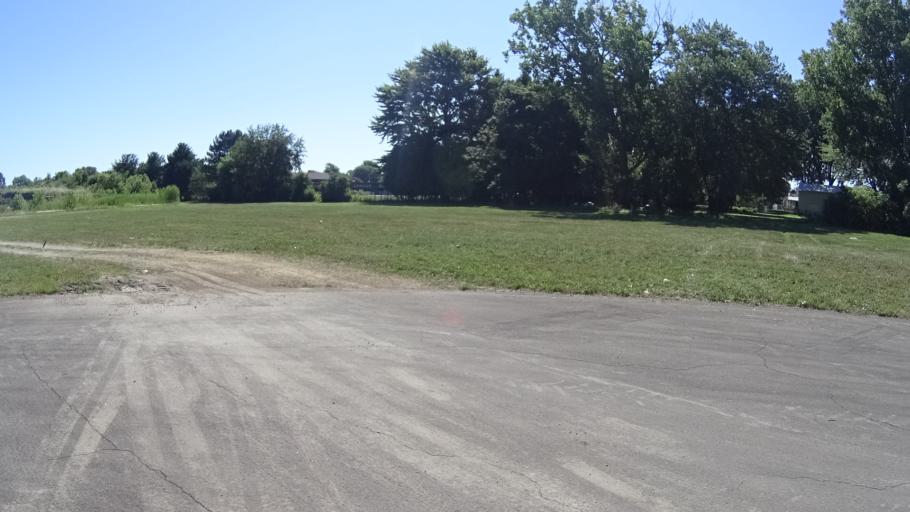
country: US
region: Ohio
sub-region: Erie County
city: Sandusky
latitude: 41.4257
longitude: -82.6736
